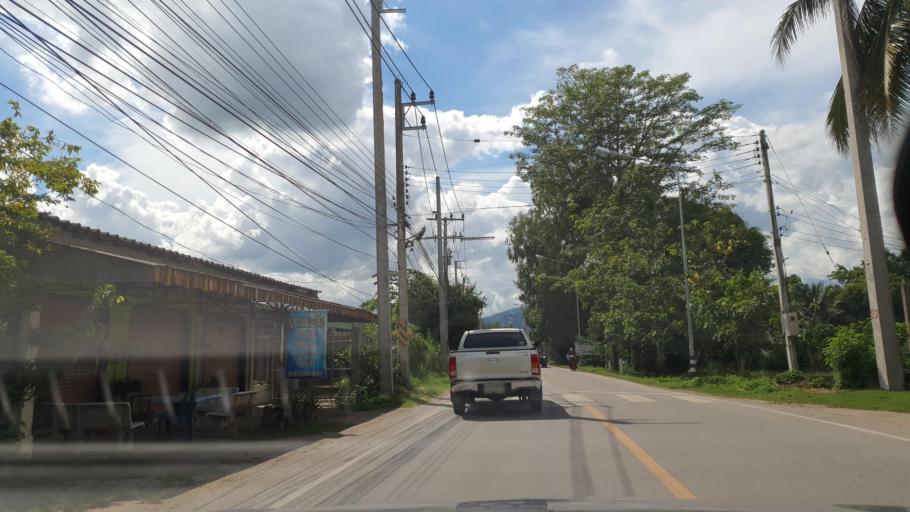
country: TH
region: Chiang Mai
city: Mae Wang
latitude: 18.6012
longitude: 98.8095
